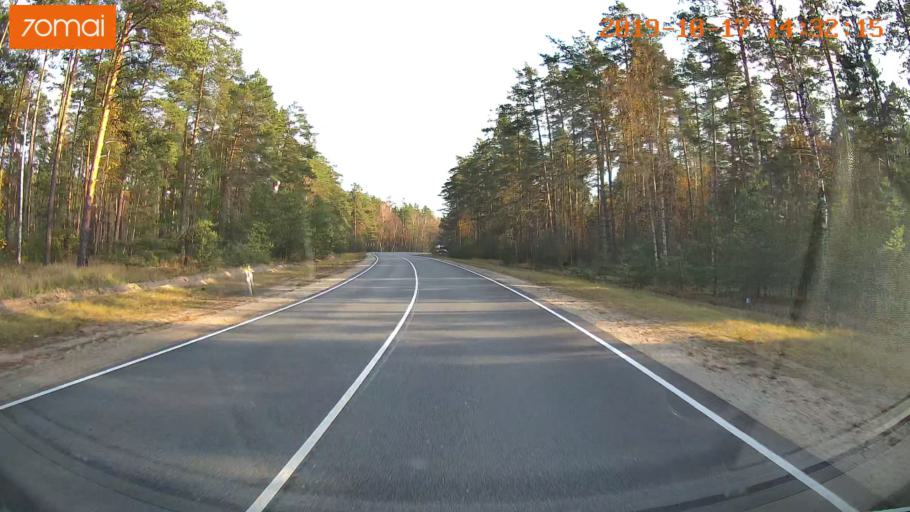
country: RU
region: Rjazan
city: Solotcha
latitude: 54.9292
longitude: 39.9762
